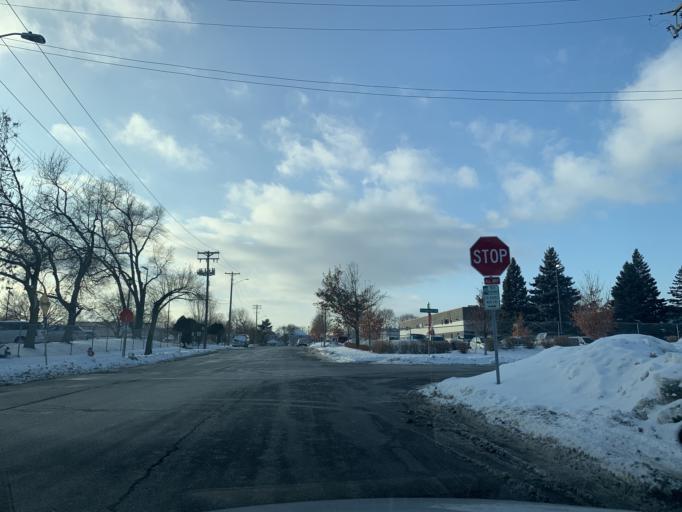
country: US
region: Minnesota
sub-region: Hennepin County
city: Minneapolis
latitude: 44.9909
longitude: -93.2954
